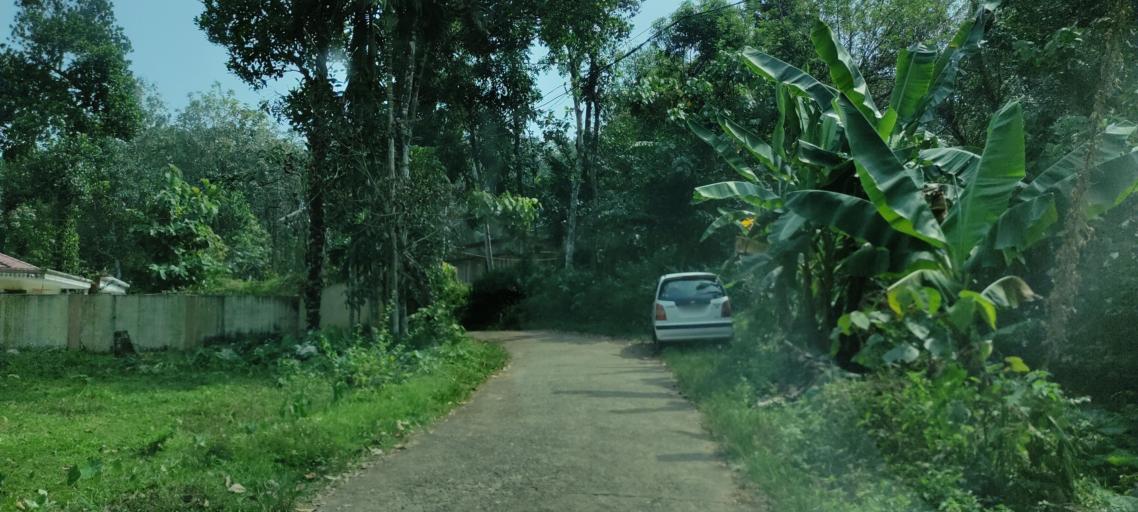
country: IN
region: Kerala
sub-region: Pattanamtitta
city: Adur
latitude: 9.2061
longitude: 76.6929
